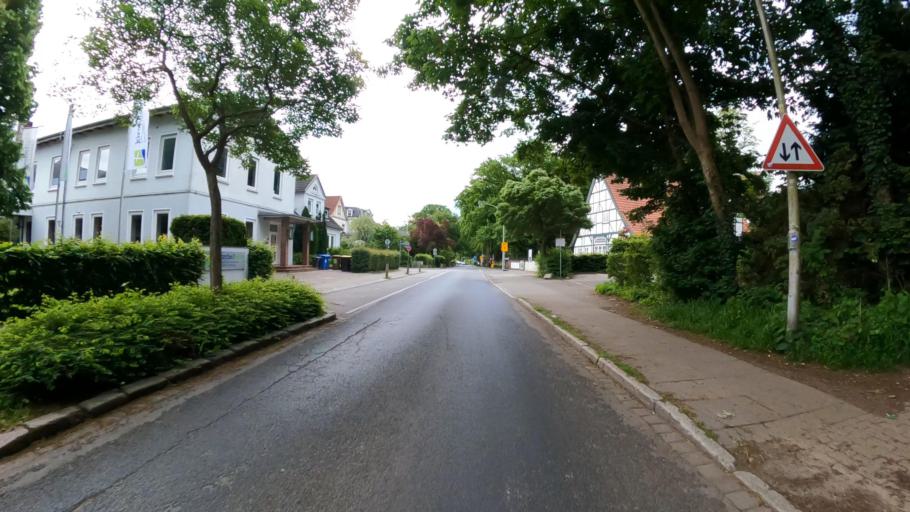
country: DE
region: Schleswig-Holstein
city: Rellingen
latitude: 53.6561
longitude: 9.8102
